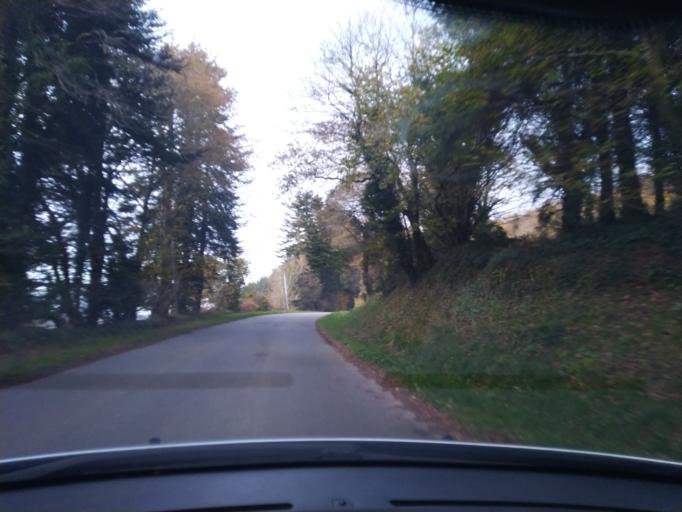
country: FR
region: Brittany
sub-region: Departement du Finistere
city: Guerlesquin
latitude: 48.5360
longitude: -3.6144
